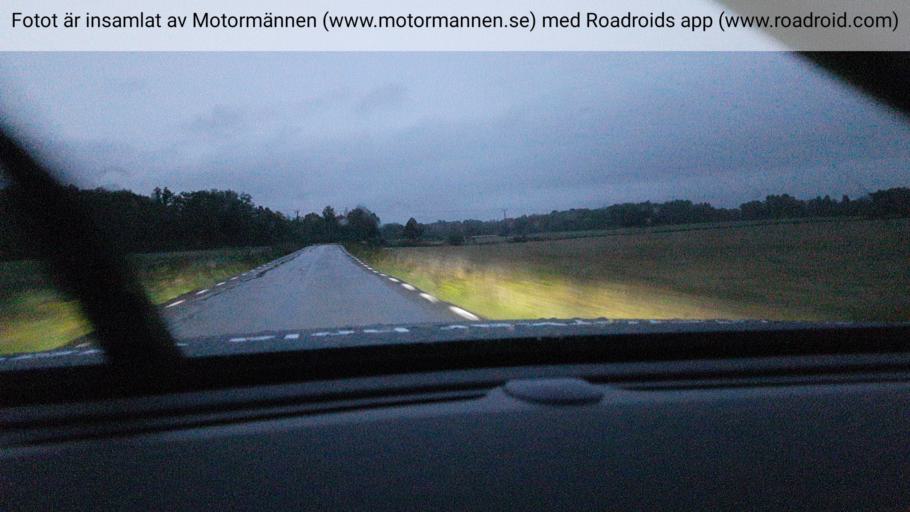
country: SE
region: Vaestra Goetaland
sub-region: Tidaholms Kommun
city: Tidaholm
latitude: 58.1860
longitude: 13.8230
